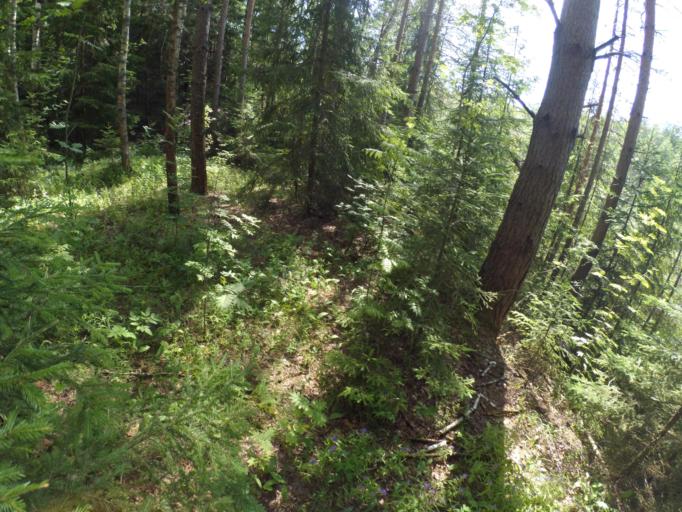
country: RU
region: Moskovskaya
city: Fosforitnyy
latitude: 55.3344
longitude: 38.9419
